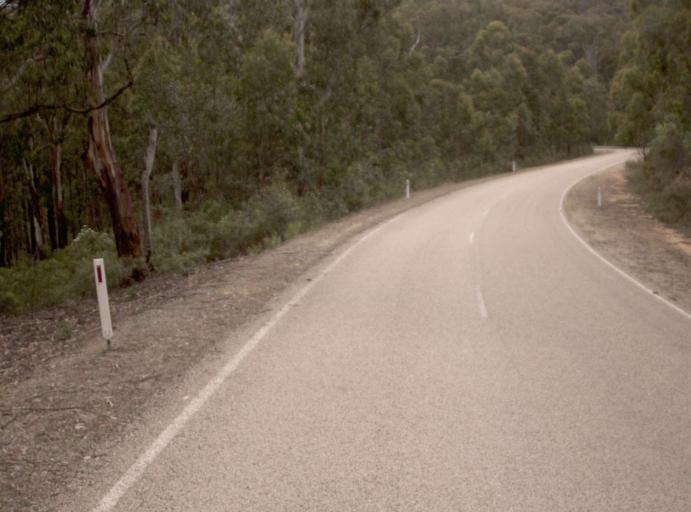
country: AU
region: Victoria
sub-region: East Gippsland
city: Bairnsdale
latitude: -37.6039
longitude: 147.1908
